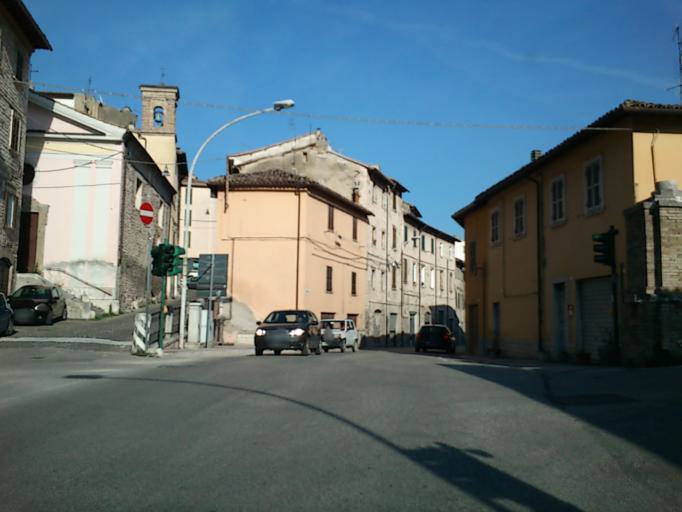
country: IT
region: The Marches
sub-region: Provincia di Pesaro e Urbino
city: Fossombrone
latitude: 43.6889
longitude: 12.8032
